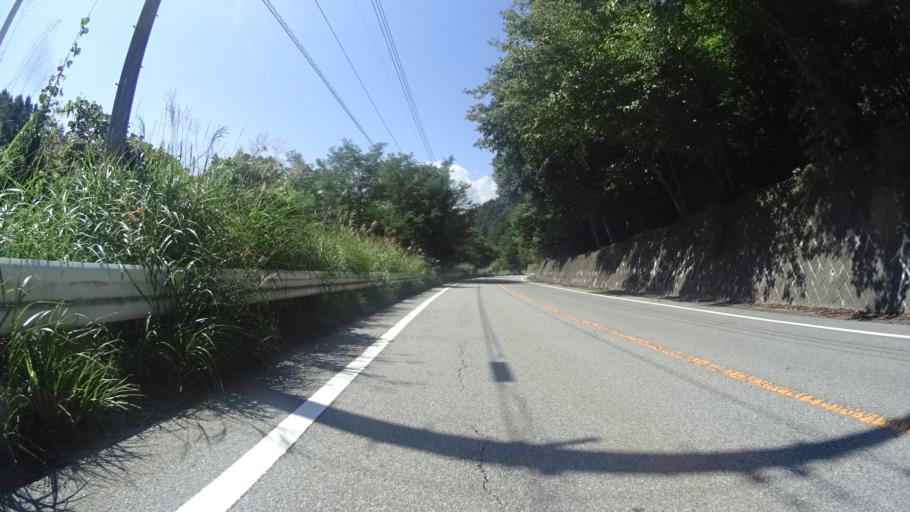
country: JP
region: Yamanashi
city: Enzan
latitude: 35.7512
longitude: 138.8073
